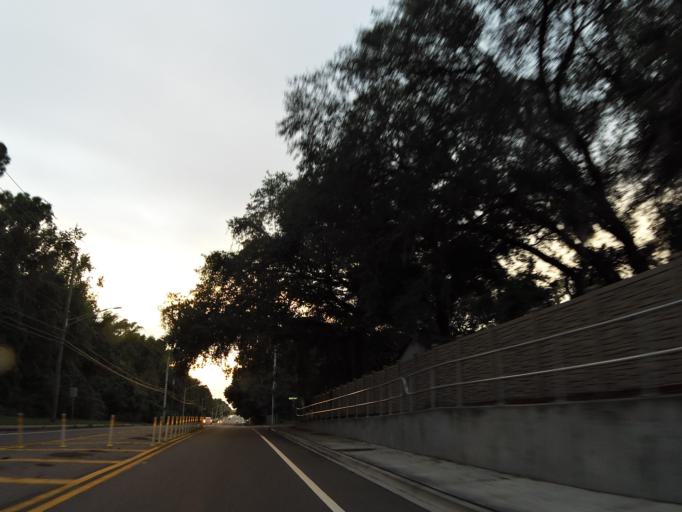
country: US
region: Florida
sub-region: Duval County
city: Jacksonville
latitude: 30.3668
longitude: -81.5669
